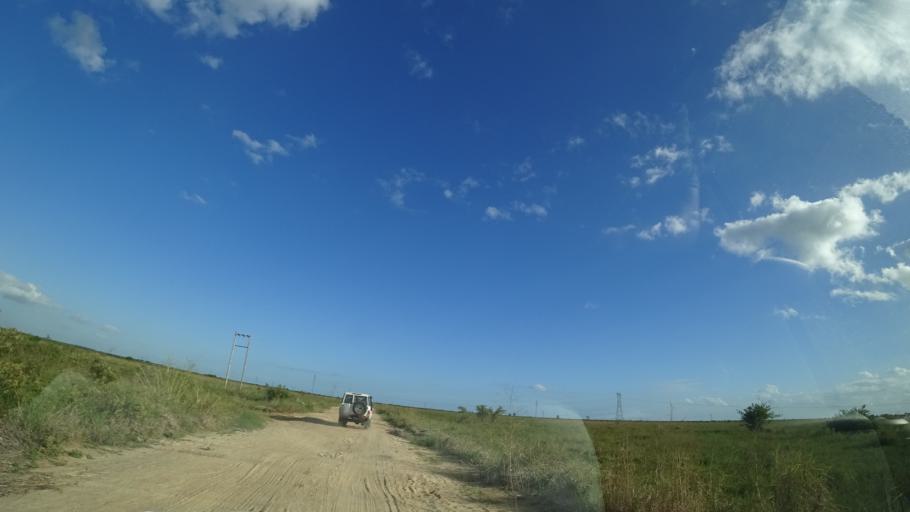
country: MZ
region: Sofala
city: Dondo
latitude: -19.4547
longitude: 34.5628
